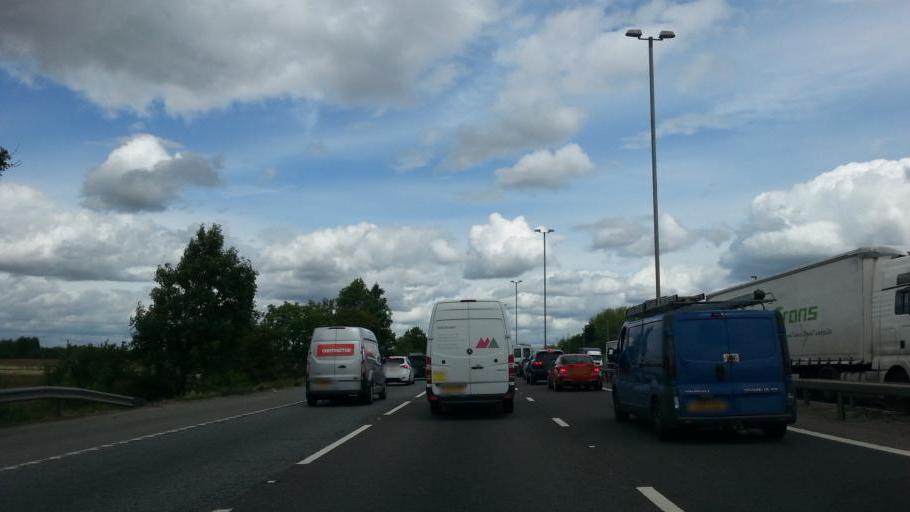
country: GB
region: England
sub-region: Essex
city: Little Hallingbury
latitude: 51.8599
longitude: 0.1892
